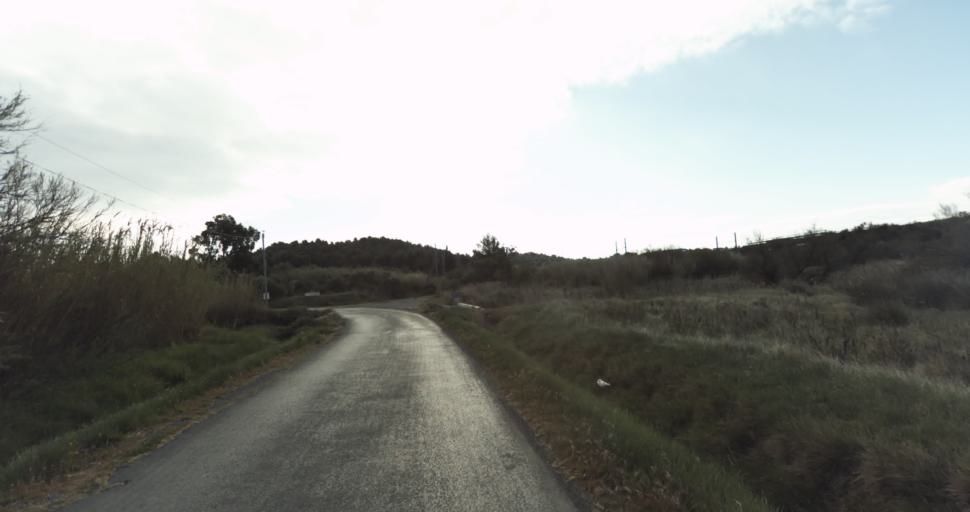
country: FR
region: Languedoc-Roussillon
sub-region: Departement de l'Aude
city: Leucate
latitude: 42.9296
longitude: 3.0093
